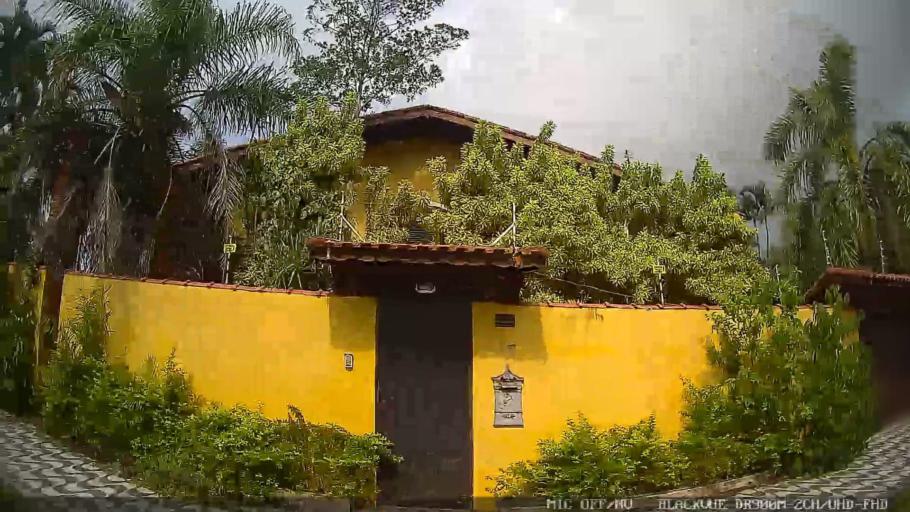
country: BR
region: Sao Paulo
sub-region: Itanhaem
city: Itanhaem
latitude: -24.2358
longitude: -46.8795
